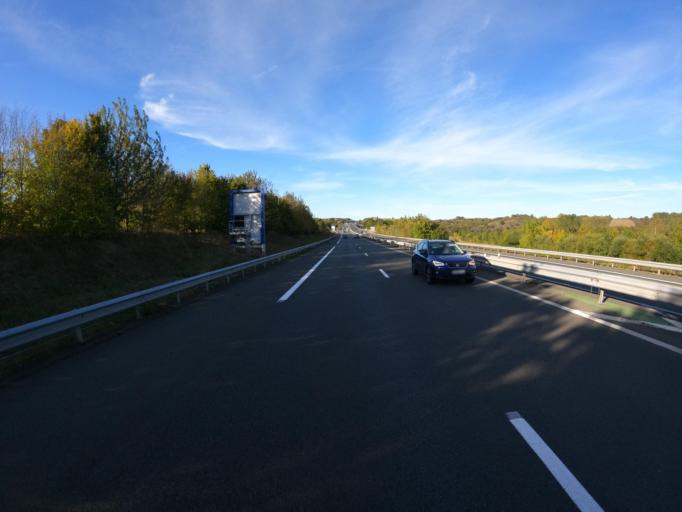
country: FR
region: Pays de la Loire
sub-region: Departement de Maine-et-Loire
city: Beaulieu-sur-Layon
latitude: 47.3055
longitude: -0.6077
